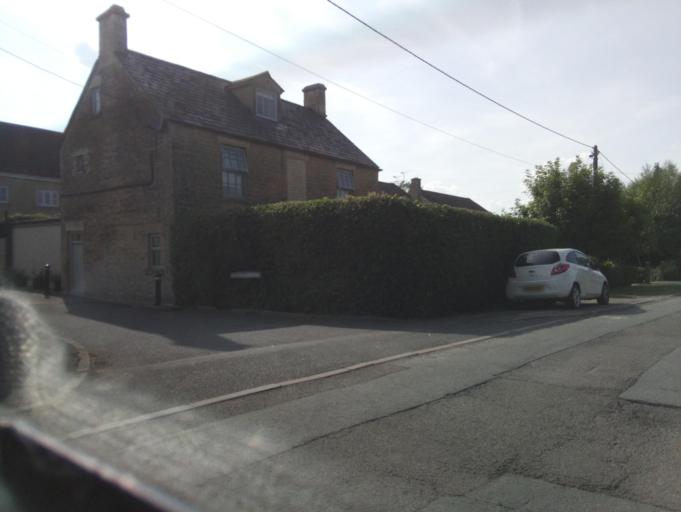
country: GB
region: England
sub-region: Wiltshire
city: Minety
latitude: 51.6126
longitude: -1.9595
